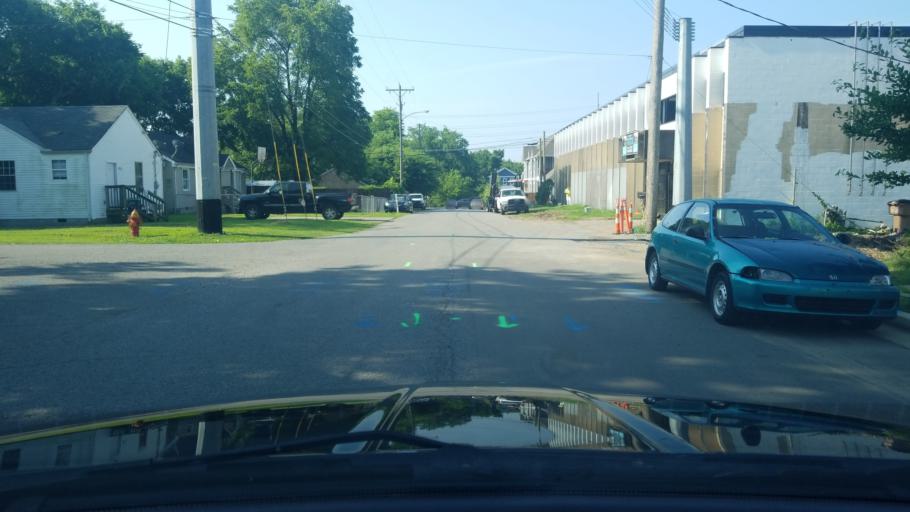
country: US
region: Tennessee
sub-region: Davidson County
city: Belle Meade
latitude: 36.1619
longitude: -86.8569
